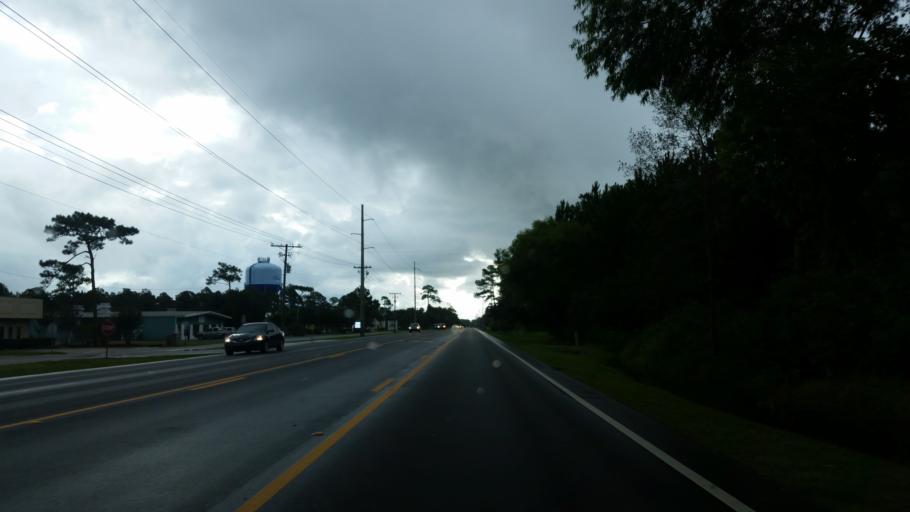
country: US
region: Alabama
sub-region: Baldwin County
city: Orange Beach
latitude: 30.2903
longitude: -87.6010
